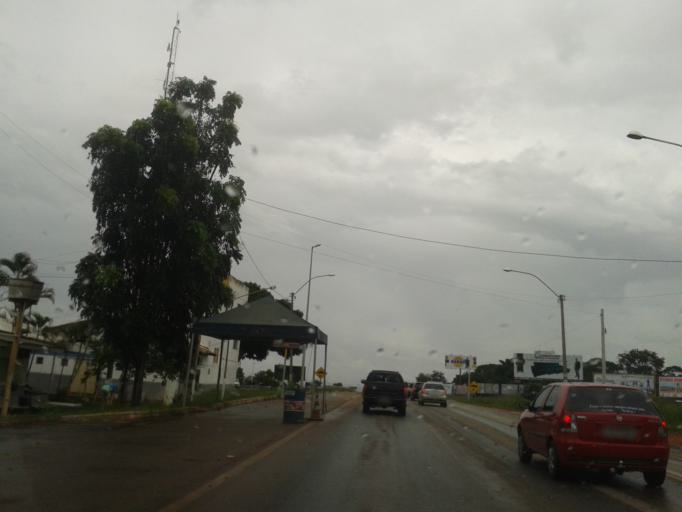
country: BR
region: Goias
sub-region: Goiania
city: Goiania
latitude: -16.6192
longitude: -49.3582
